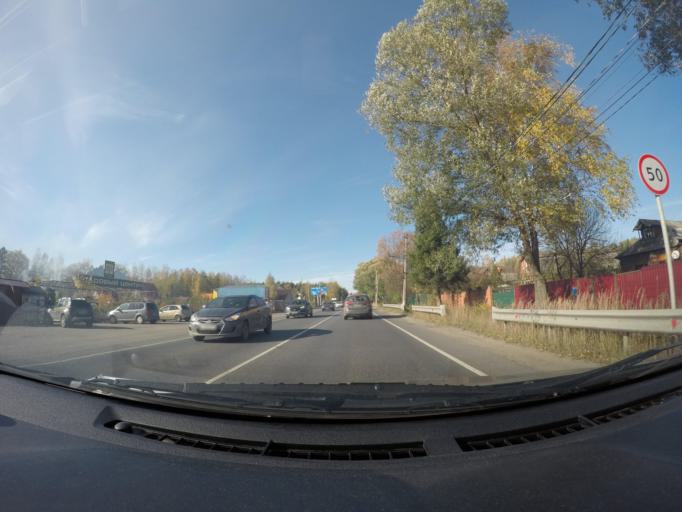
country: RU
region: Moskovskaya
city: Gzhel'
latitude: 55.6366
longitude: 38.3013
